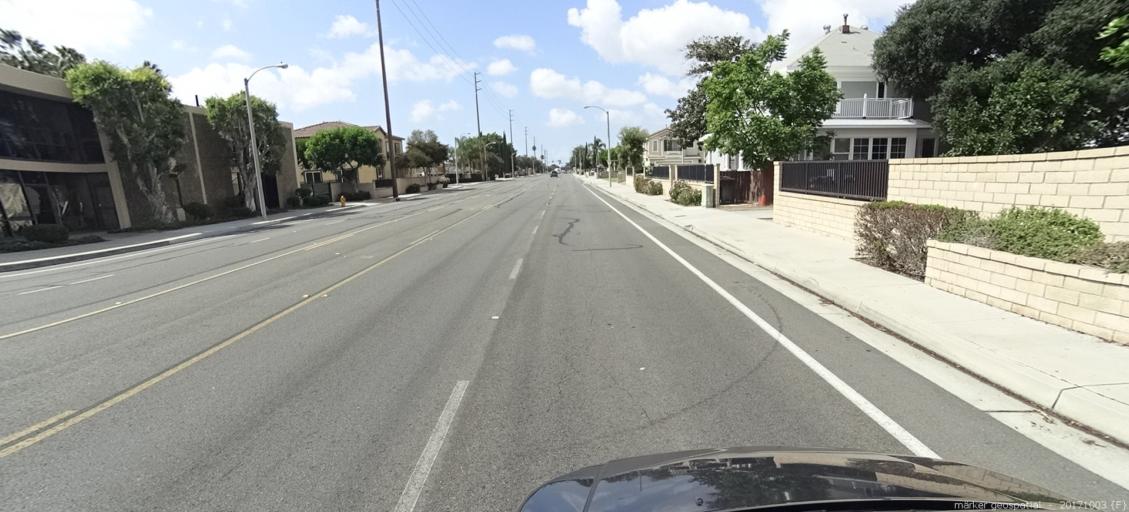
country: US
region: California
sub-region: Orange County
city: Garden Grove
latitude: 33.7670
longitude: -117.9309
